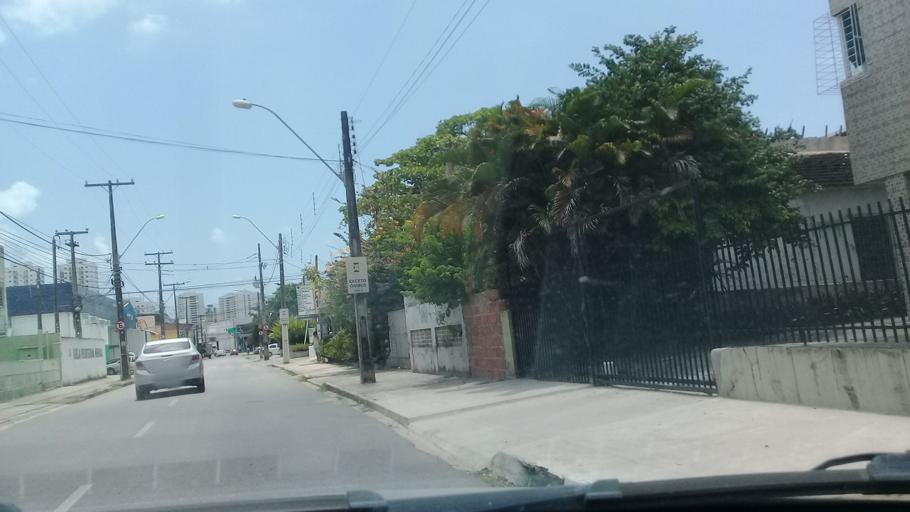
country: BR
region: Pernambuco
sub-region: Recife
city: Recife
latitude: -8.1072
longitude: -34.9138
